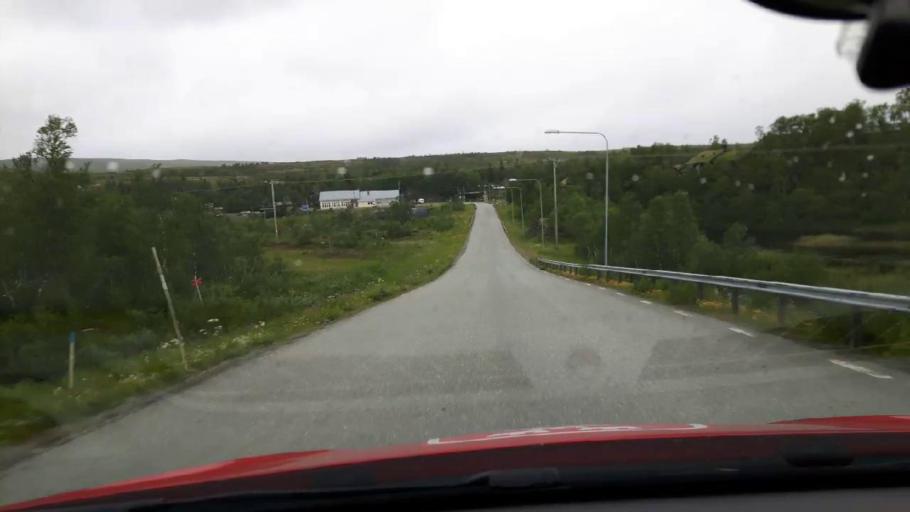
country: NO
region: Nord-Trondelag
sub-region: Meraker
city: Meraker
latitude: 63.3109
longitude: 12.1110
